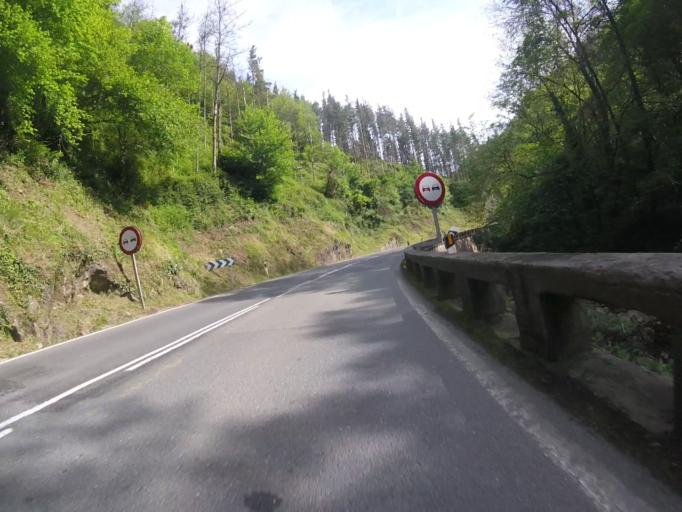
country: ES
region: Basque Country
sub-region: Provincia de Guipuzcoa
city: Azkoitia
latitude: 43.1452
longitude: -2.3466
